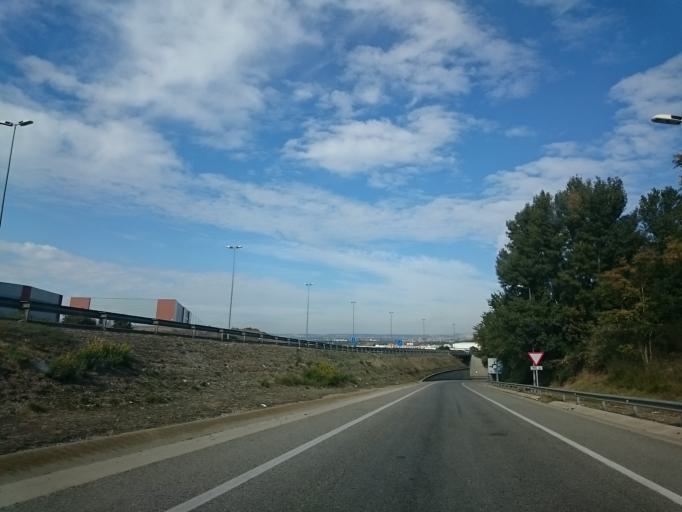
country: ES
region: Catalonia
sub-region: Provincia de Lleida
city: Alcoletge
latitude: 41.6168
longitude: 0.6670
